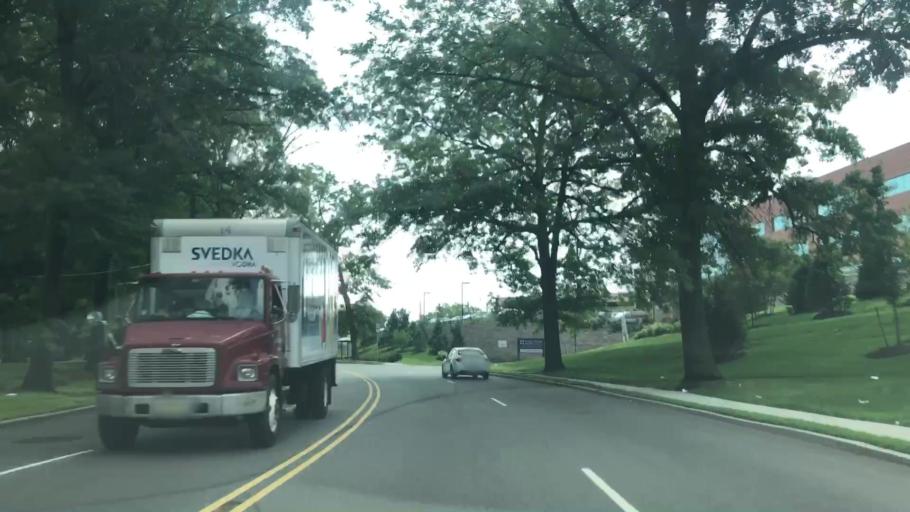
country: US
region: New Jersey
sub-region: Essex County
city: Bloomfield
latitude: 40.7867
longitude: -74.1749
